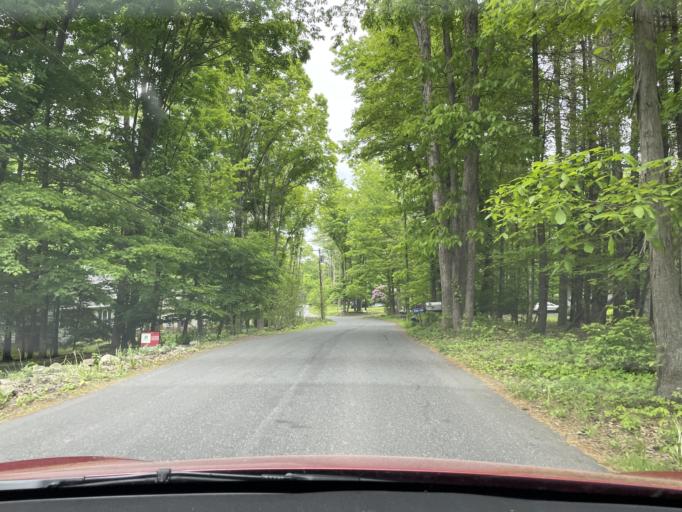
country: US
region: New York
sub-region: Ulster County
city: West Hurley
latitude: 42.0119
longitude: -74.1001
